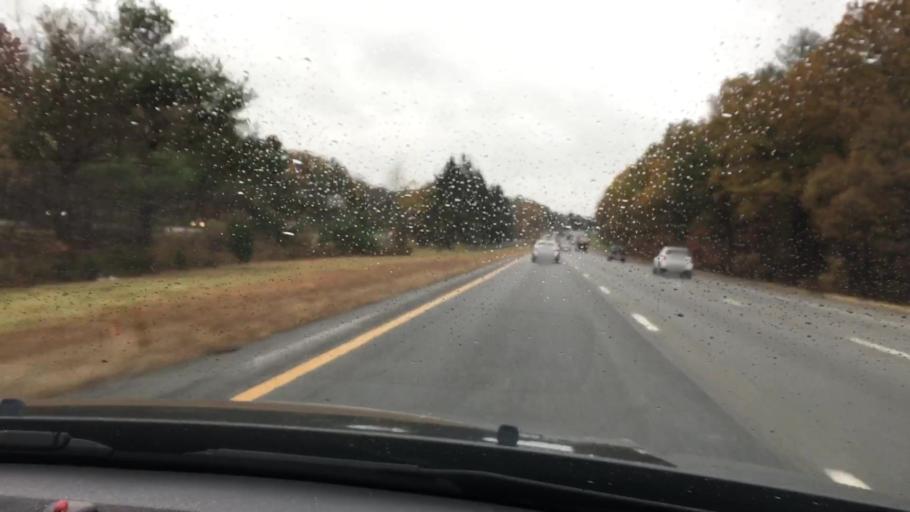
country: US
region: Massachusetts
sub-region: Middlesex County
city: Westford
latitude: 42.5634
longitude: -71.4338
